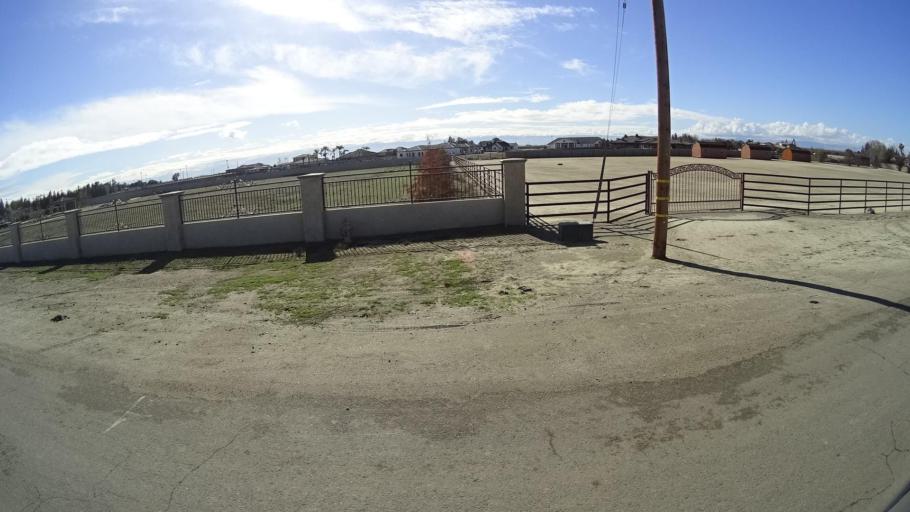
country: US
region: California
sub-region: Kern County
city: Rosedale
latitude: 35.3617
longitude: -119.2029
